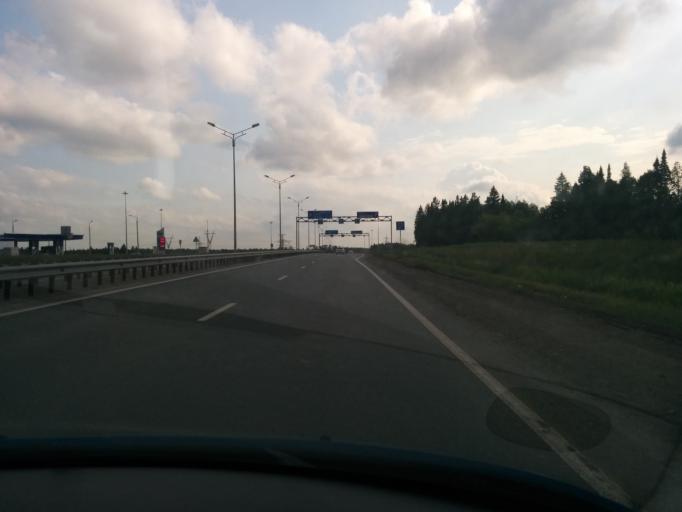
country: RU
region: Perm
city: Ferma
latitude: 58.0029
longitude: 56.3908
